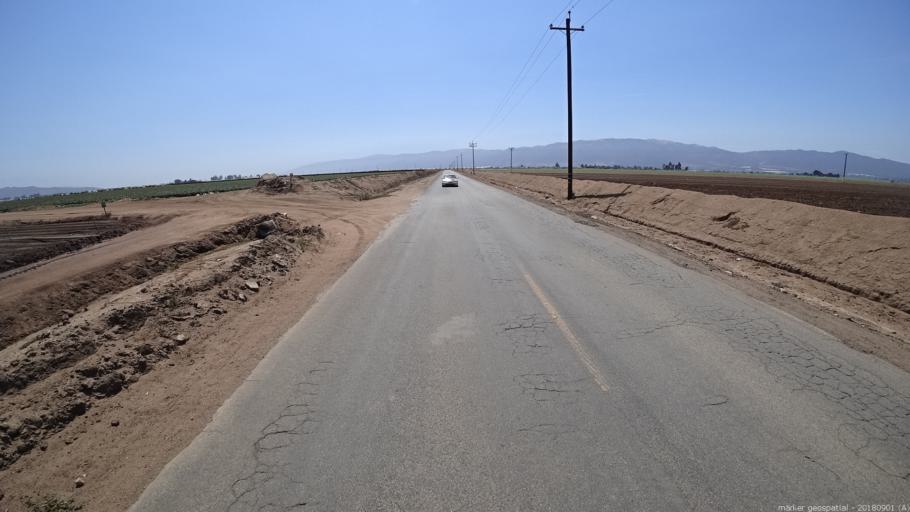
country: US
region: California
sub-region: Monterey County
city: Chualar
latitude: 36.6400
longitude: -121.5426
